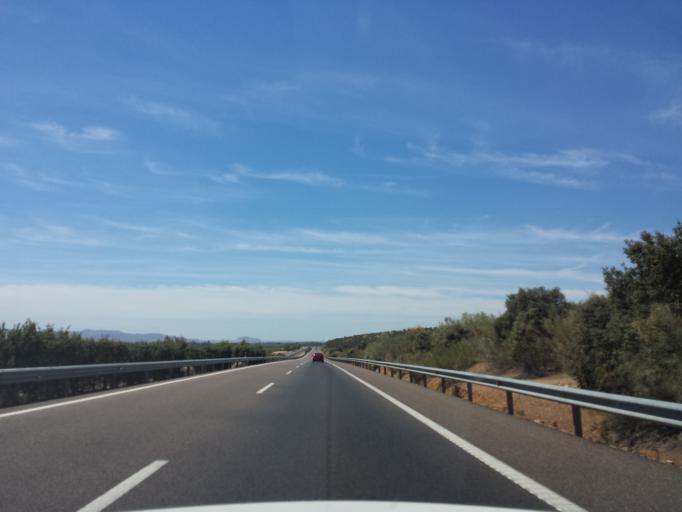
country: ES
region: Extremadura
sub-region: Provincia de Badajoz
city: San Pedro de Merida
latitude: 38.9708
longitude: -6.1503
